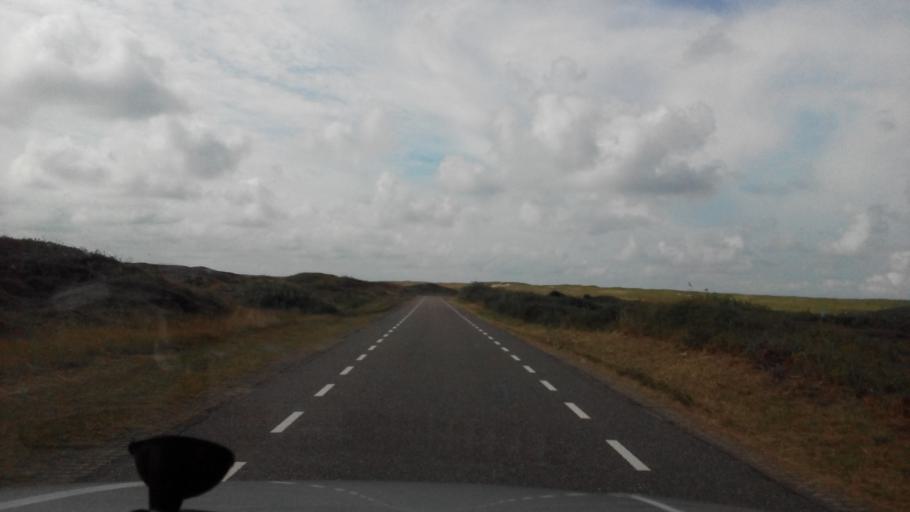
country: NL
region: North Holland
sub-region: Gemeente Texel
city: Den Burg
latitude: 53.0405
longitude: 4.7189
